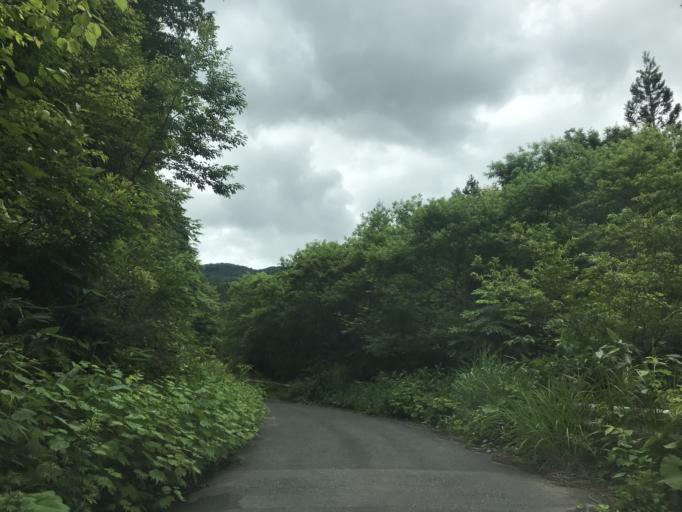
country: JP
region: Iwate
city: Ichinoseki
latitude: 38.9506
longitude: 140.8773
